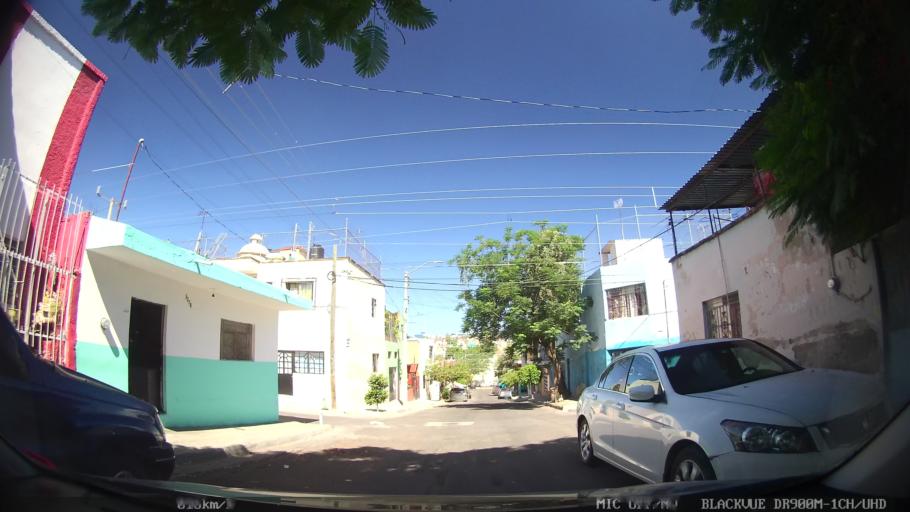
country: MX
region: Jalisco
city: Tlaquepaque
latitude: 20.6974
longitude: -103.2829
